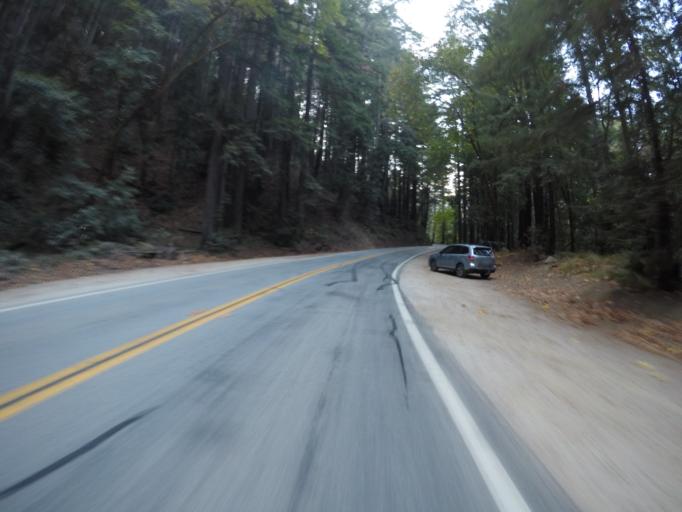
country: US
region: California
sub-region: Santa Cruz County
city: Pasatiempo
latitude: 37.0125
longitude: -122.0551
